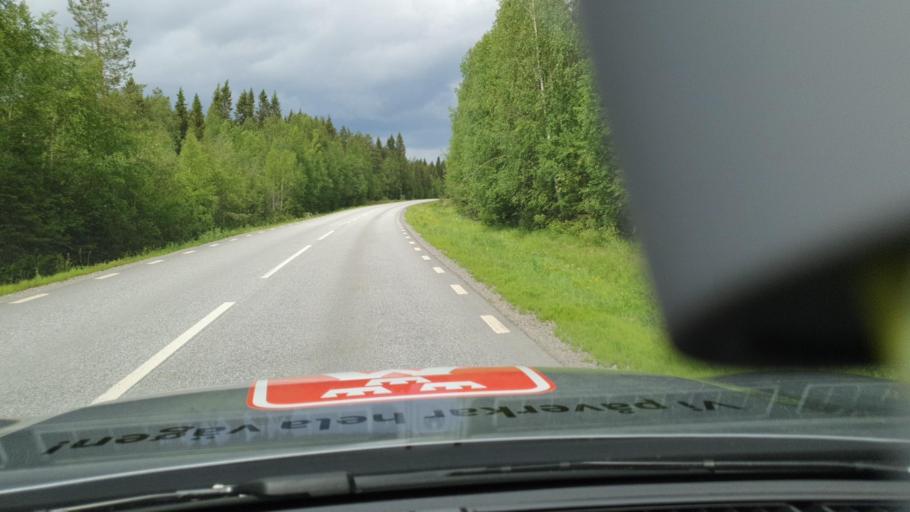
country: SE
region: Norrbotten
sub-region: Lulea Kommun
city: Lulea
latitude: 65.6851
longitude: 22.2103
